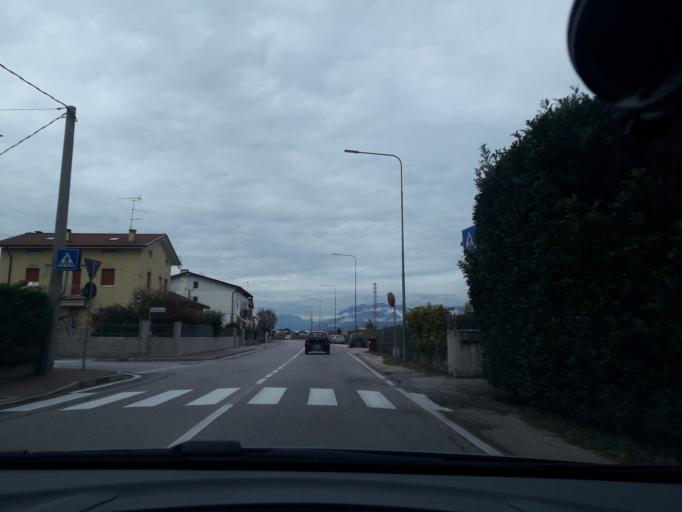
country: IT
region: Friuli Venezia Giulia
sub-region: Provincia di Udine
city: Colugna
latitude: 46.0879
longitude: 13.2150
